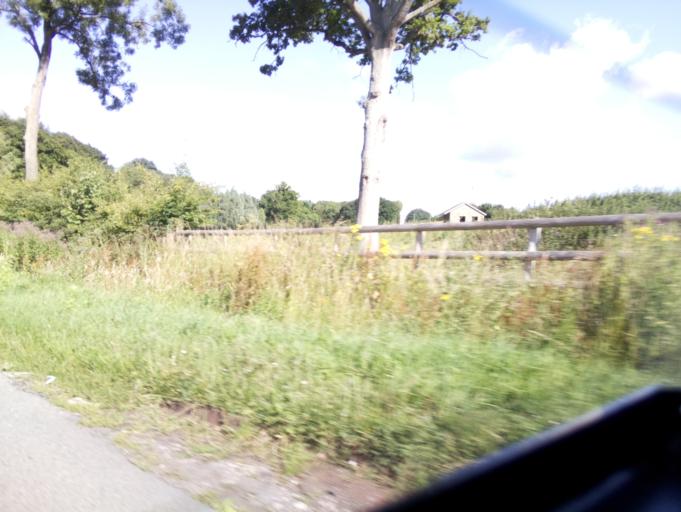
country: GB
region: England
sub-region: Herefordshire
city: Linton
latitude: 51.9327
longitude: -2.4993
